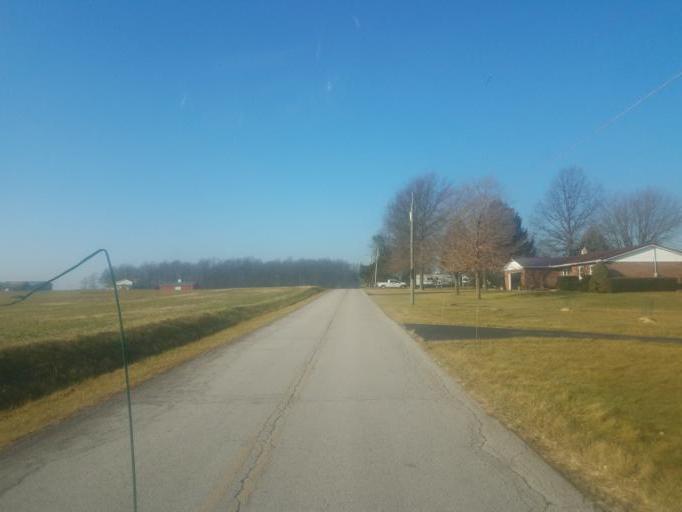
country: US
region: Ohio
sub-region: Seneca County
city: Tiffin
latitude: 41.0448
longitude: -83.0119
